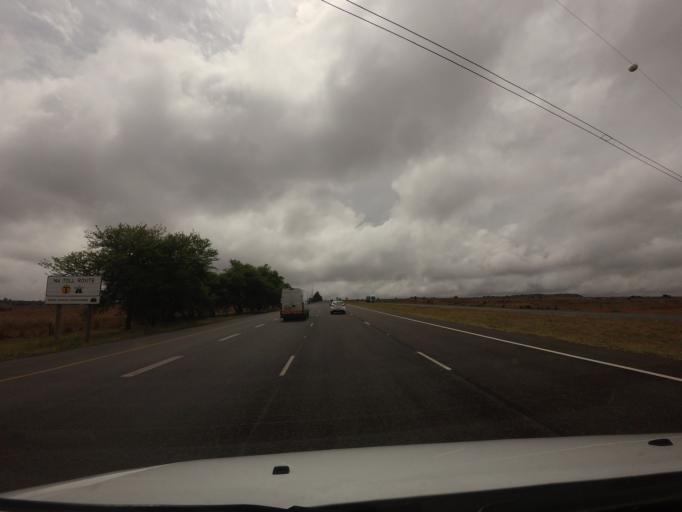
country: ZA
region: Mpumalanga
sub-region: Nkangala District Municipality
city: Middelburg
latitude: -25.8415
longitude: 29.4094
